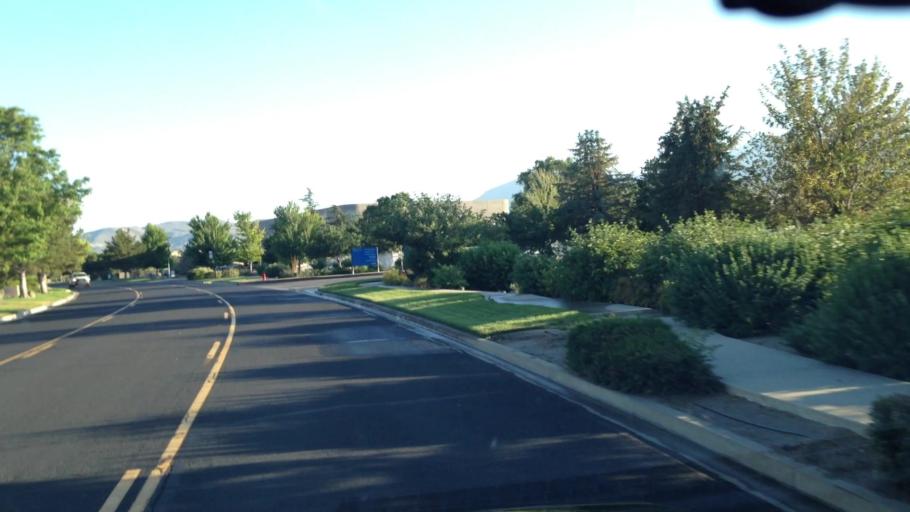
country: US
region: Nevada
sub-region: Washoe County
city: Sparks
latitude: 39.4488
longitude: -119.7618
